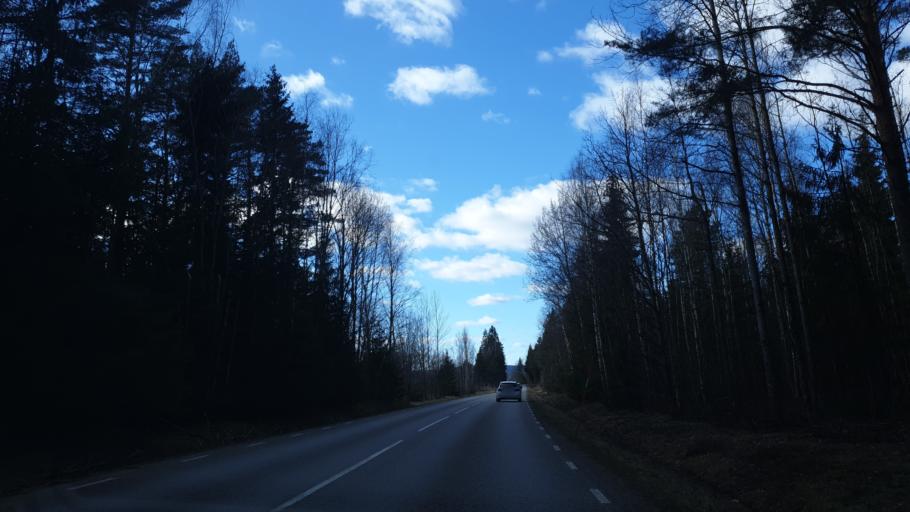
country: SE
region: OErebro
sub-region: Orebro Kommun
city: Garphyttan
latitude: 59.3355
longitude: 15.0762
